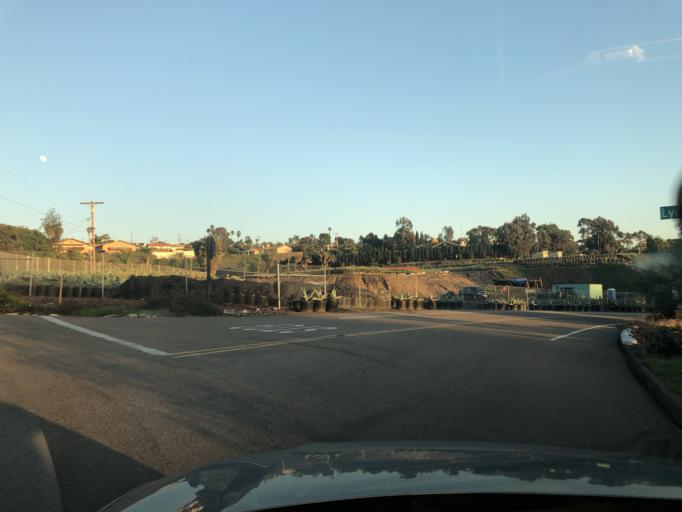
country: US
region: California
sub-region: San Diego County
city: Bonita
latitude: 32.6459
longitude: -117.0560
